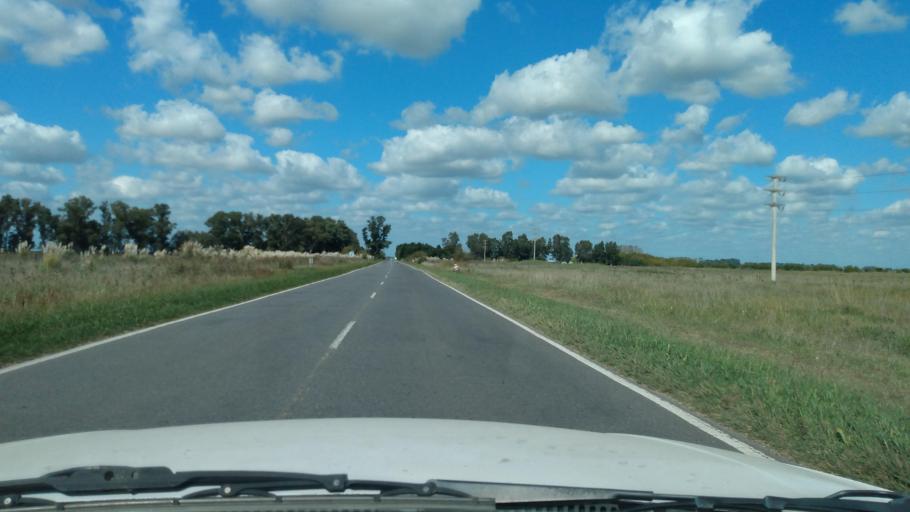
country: AR
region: Buenos Aires
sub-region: Partido de Navarro
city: Navarro
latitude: -34.8826
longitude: -59.3404
